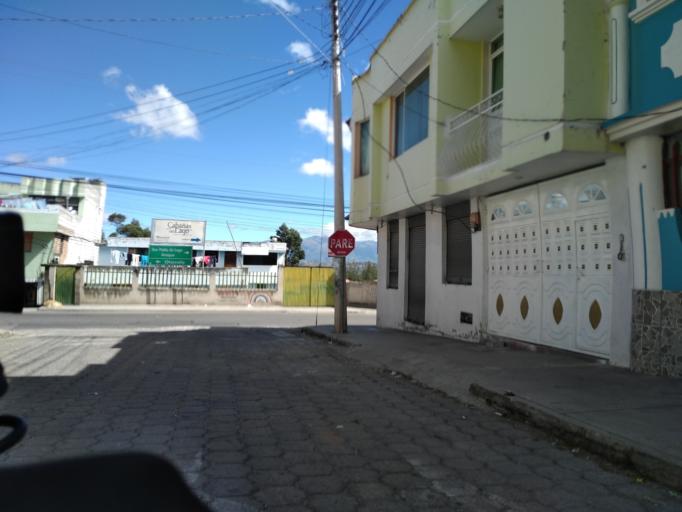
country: EC
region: Imbabura
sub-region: Canton Otavalo
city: Otavalo
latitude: 0.1802
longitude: -78.2034
